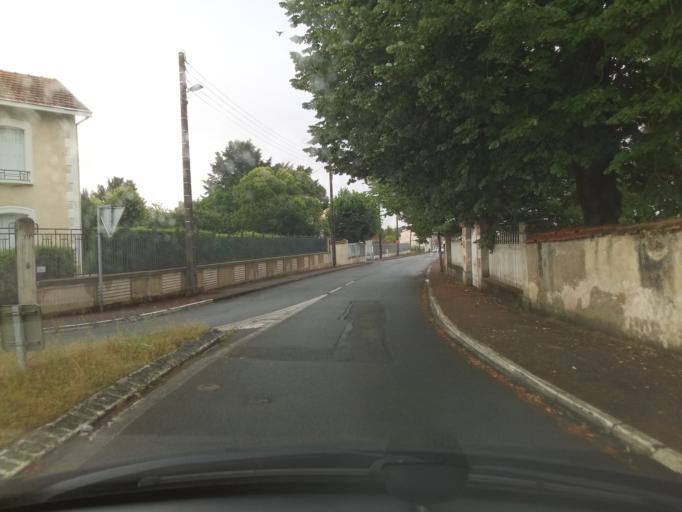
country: FR
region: Poitou-Charentes
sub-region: Departement de la Charente-Maritime
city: Surgeres
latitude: 46.1121
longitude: -0.7575
